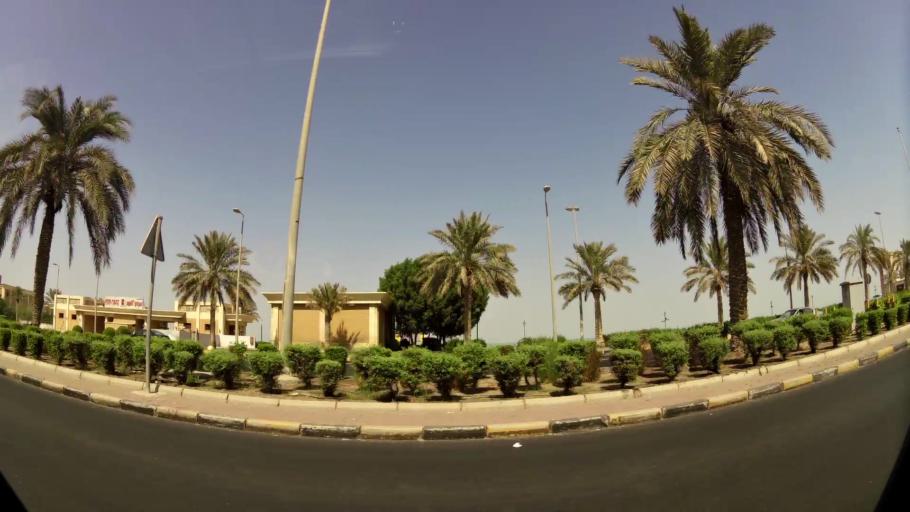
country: KW
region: Al Asimah
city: Kuwait City
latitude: 29.3904
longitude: 47.9931
